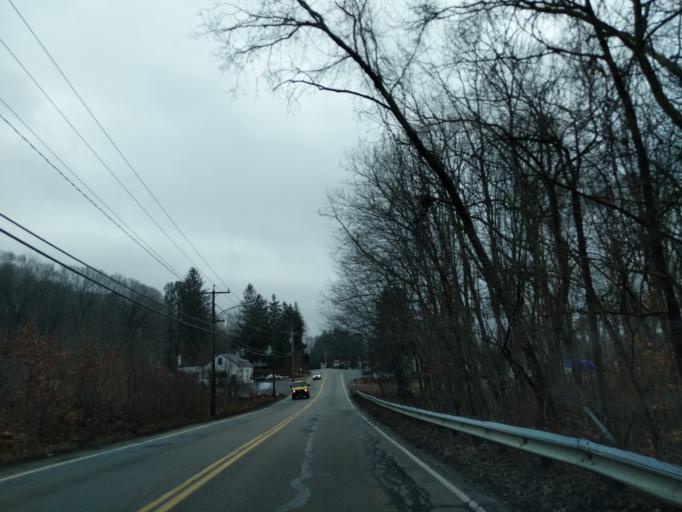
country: US
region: Massachusetts
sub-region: Worcester County
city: Webster
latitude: 42.0587
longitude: -71.8439
